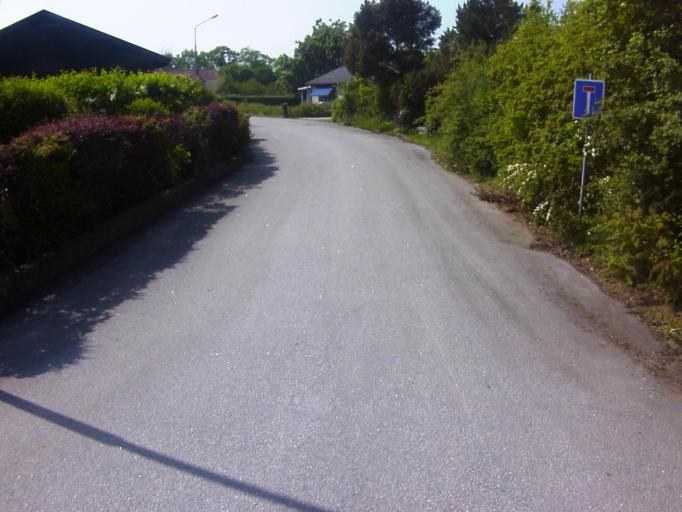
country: SE
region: Blekinge
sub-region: Karlshamns Kommun
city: Morrum
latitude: 56.1166
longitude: 14.6756
